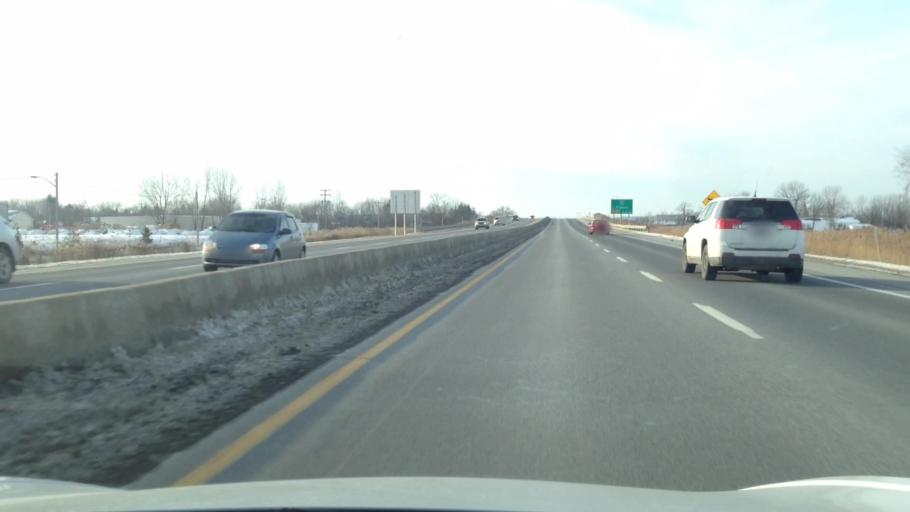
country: CA
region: Quebec
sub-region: Monteregie
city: Rigaud
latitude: 45.4850
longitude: -74.2944
